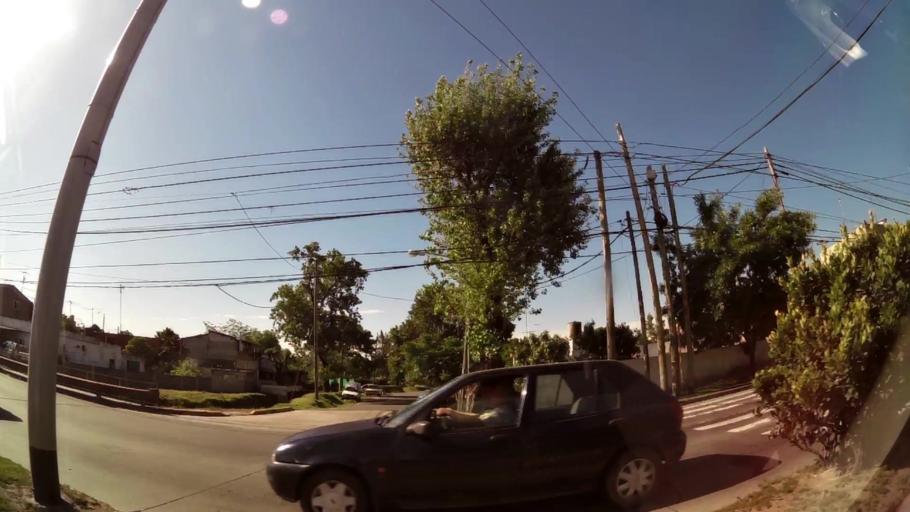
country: AR
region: Buenos Aires
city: Santa Catalina - Dique Lujan
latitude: -34.4783
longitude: -58.6708
